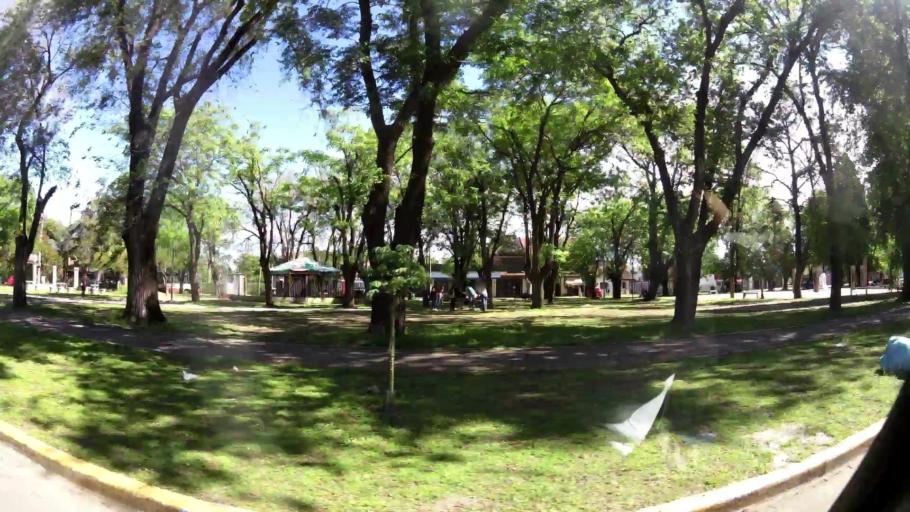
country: AR
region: Buenos Aires
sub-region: Partido de Almirante Brown
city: Adrogue
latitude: -34.7973
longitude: -58.3583
